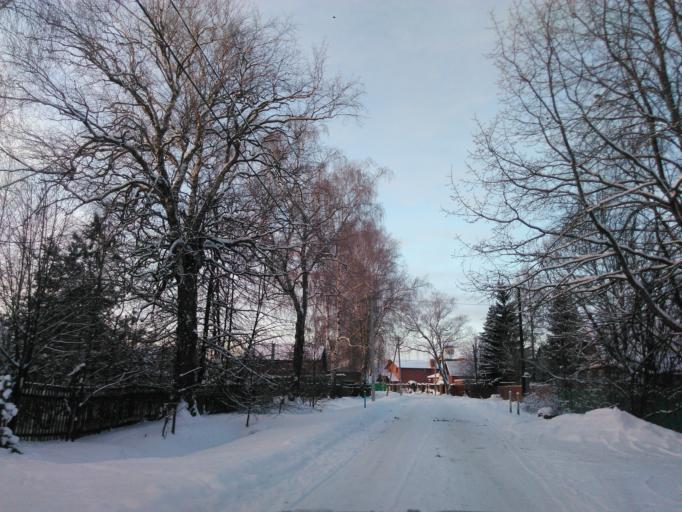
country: RU
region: Tverskaya
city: Zavidovo
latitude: 56.6363
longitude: 36.6180
